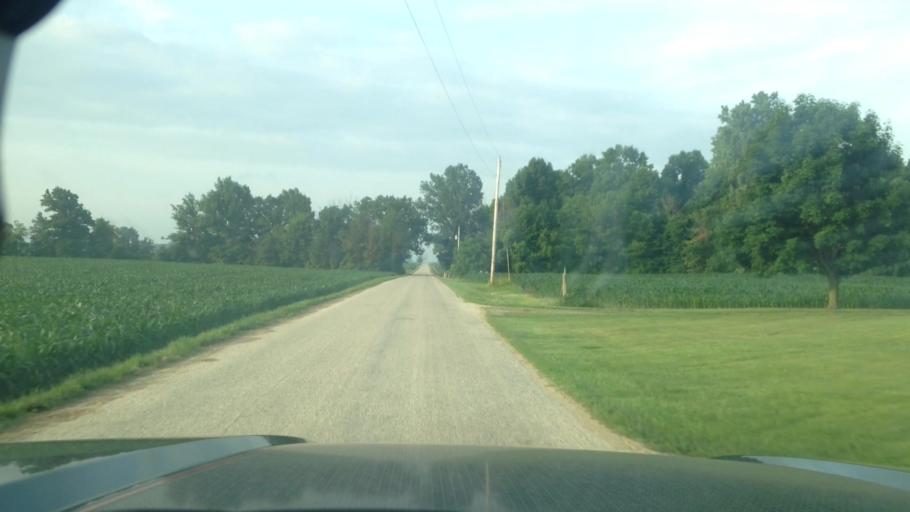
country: US
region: Indiana
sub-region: Randolph County
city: Union City
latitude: 40.2423
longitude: -84.8625
